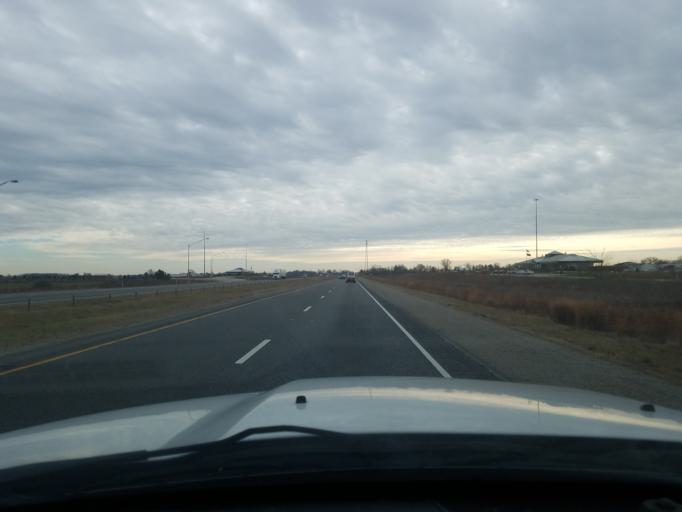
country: US
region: Indiana
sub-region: Grant County
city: Fairmount
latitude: 40.3590
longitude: -85.5590
